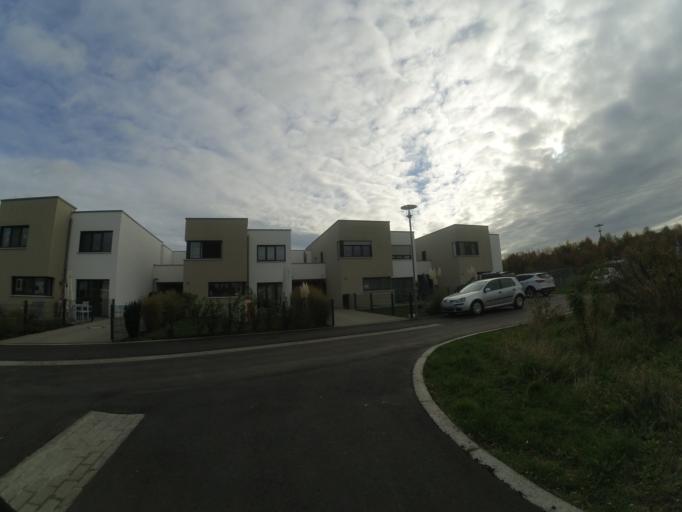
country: DE
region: Bavaria
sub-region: Swabia
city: Neu-Ulm
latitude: 48.4002
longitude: 10.0295
